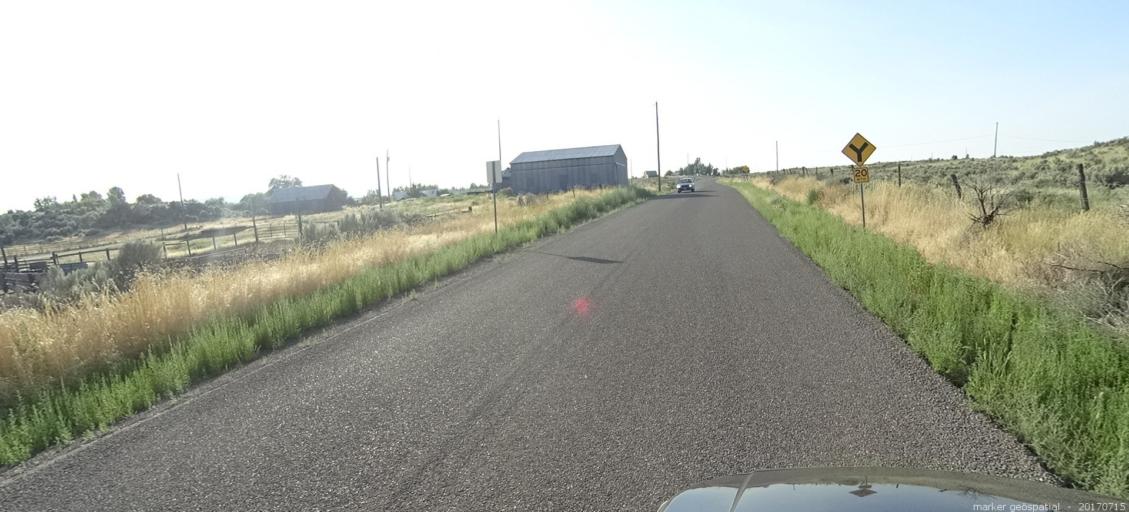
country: US
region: Idaho
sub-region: Ada County
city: Boise
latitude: 43.3891
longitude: -115.9746
